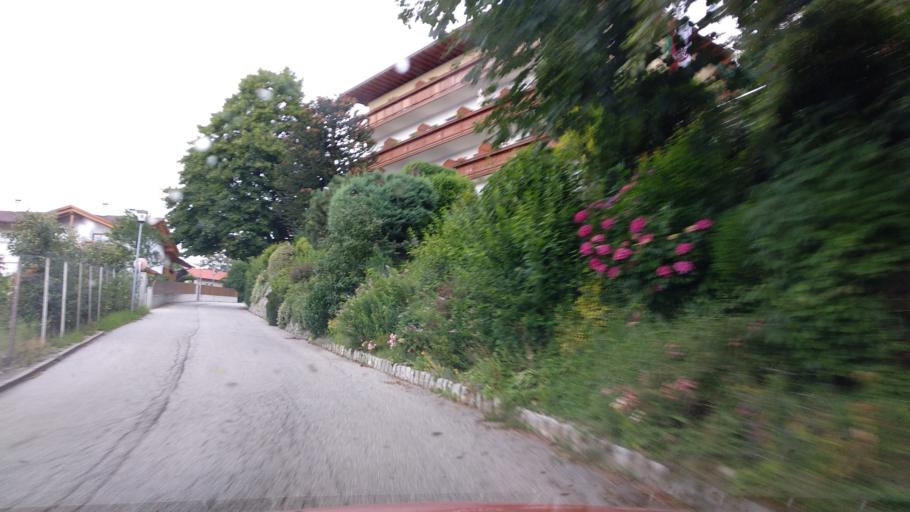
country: IT
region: Trentino-Alto Adige
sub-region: Bolzano
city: Scena
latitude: 46.6968
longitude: 11.2013
